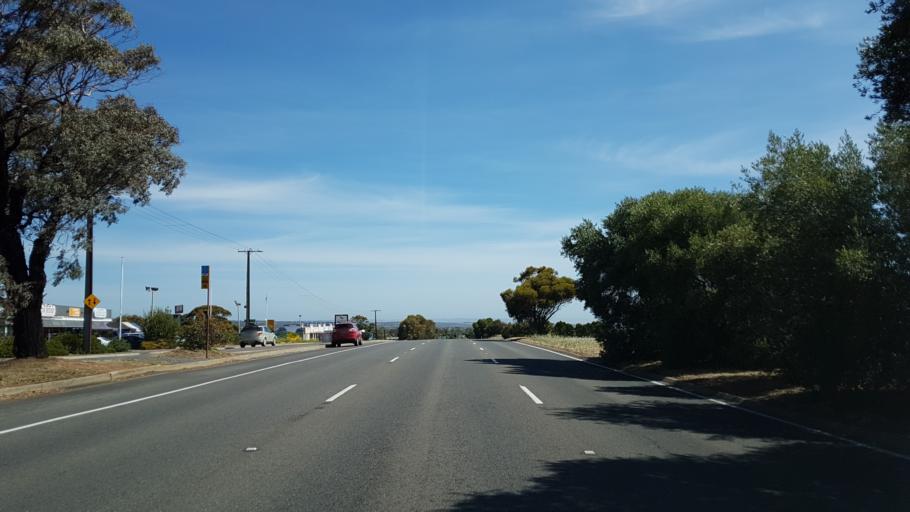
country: AU
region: South Australia
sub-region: Marion
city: Trott Park
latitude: -35.0675
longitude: 138.5549
